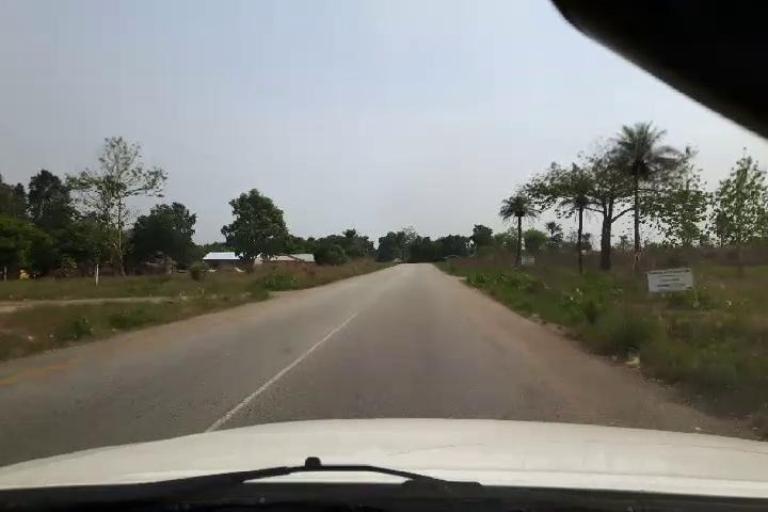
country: SL
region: Southern Province
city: Largo
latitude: 8.3124
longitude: -12.2166
